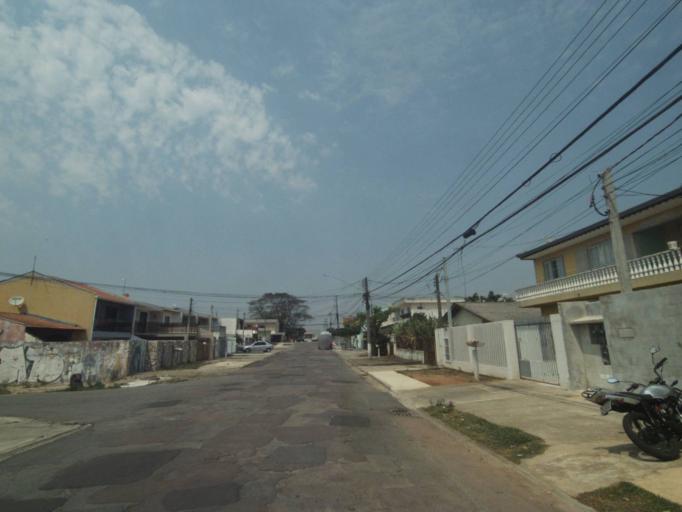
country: BR
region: Parana
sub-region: Sao Jose Dos Pinhais
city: Sao Jose dos Pinhais
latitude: -25.5347
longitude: -49.2447
